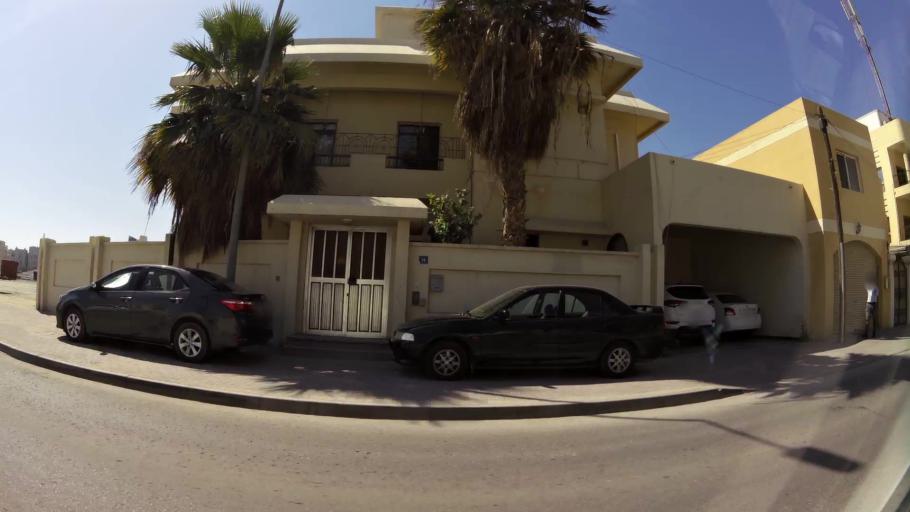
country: BH
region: Manama
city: Manama
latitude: 26.2059
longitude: 50.5890
